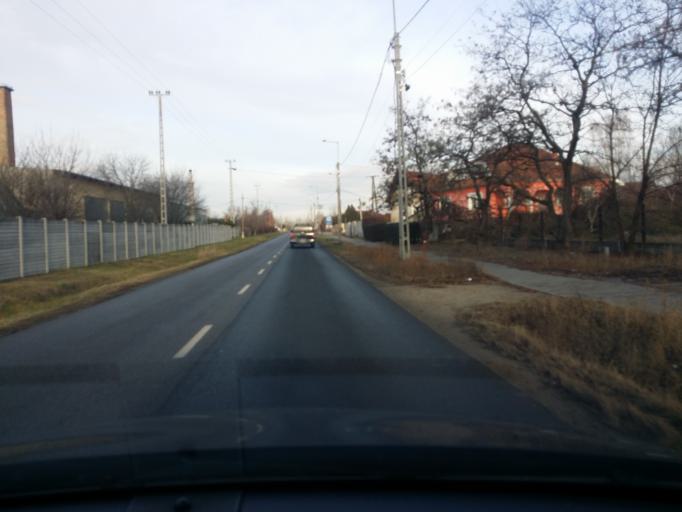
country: HU
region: Pest
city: Alsonemedi
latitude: 47.3228
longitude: 19.1494
